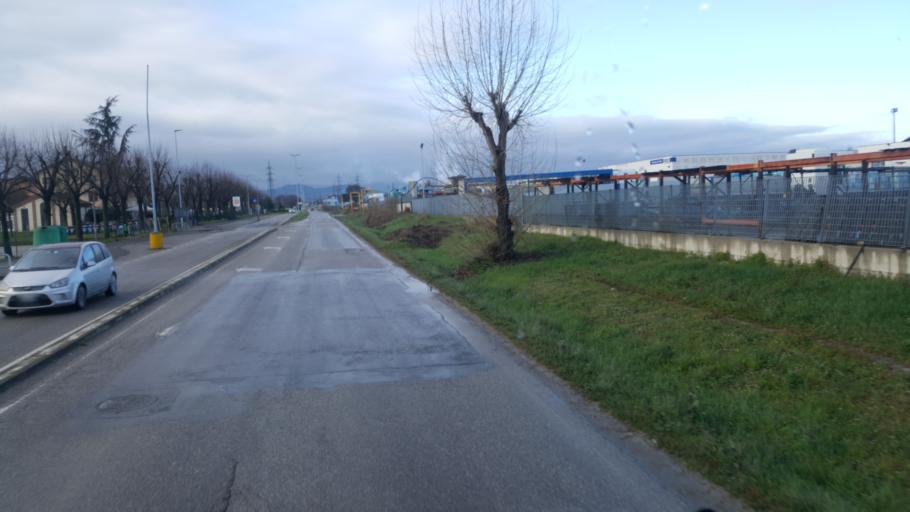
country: IT
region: Emilia-Romagna
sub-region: Provincia di Modena
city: Sassuolo
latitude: 44.5619
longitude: 10.7903
